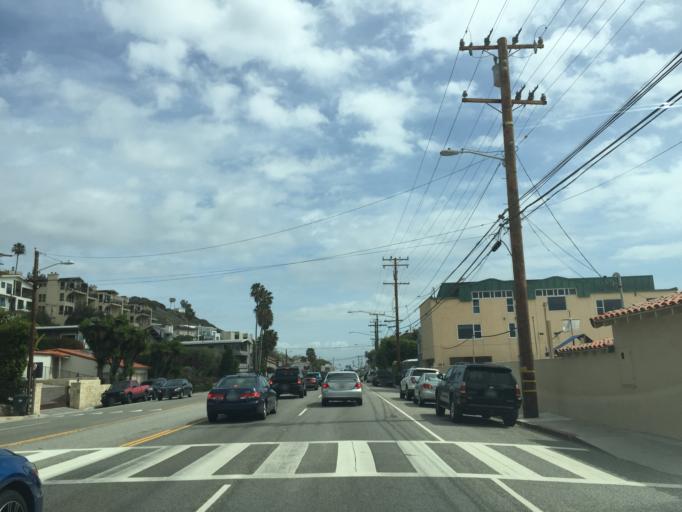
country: US
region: California
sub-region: Los Angeles County
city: Las Flores
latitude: 34.0380
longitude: -118.6418
